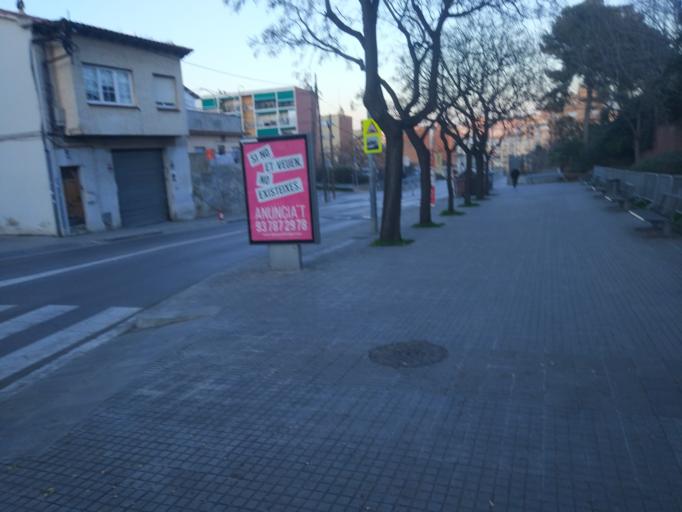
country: ES
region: Catalonia
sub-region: Provincia de Barcelona
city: Rubi
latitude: 41.4903
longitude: 2.0257
